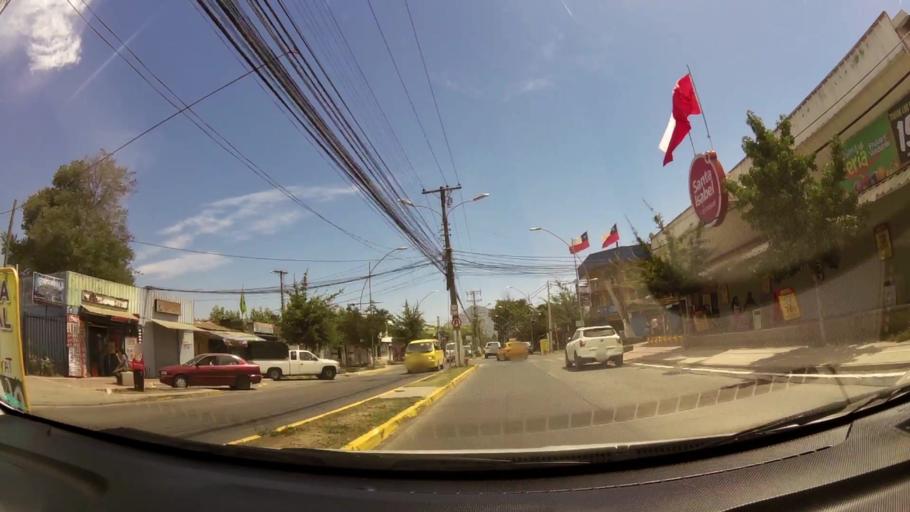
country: CL
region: O'Higgins
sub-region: Provincia de Cachapoal
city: Graneros
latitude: -33.9814
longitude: -70.7126
